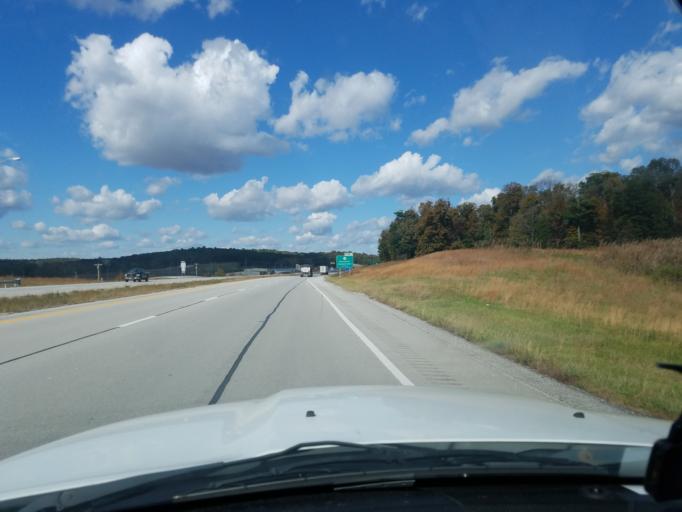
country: US
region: Kentucky
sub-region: Butler County
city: Morgantown
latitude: 37.2062
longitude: -86.7049
